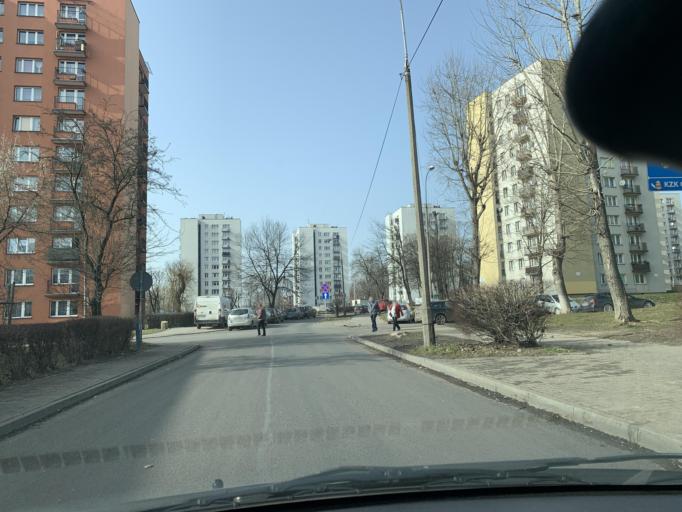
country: PL
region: Silesian Voivodeship
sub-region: Bytom
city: Bytom
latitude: 50.3351
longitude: 18.8879
